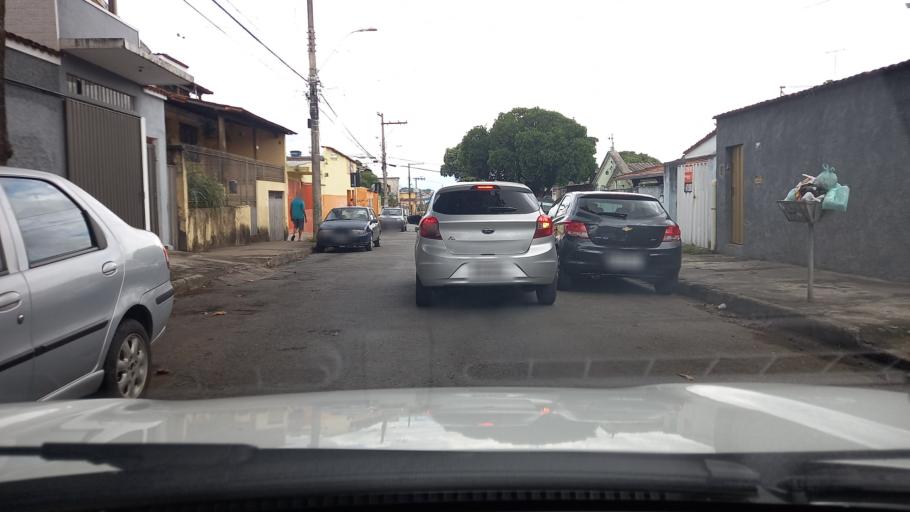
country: BR
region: Minas Gerais
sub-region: Contagem
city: Contagem
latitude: -19.9044
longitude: -44.0077
